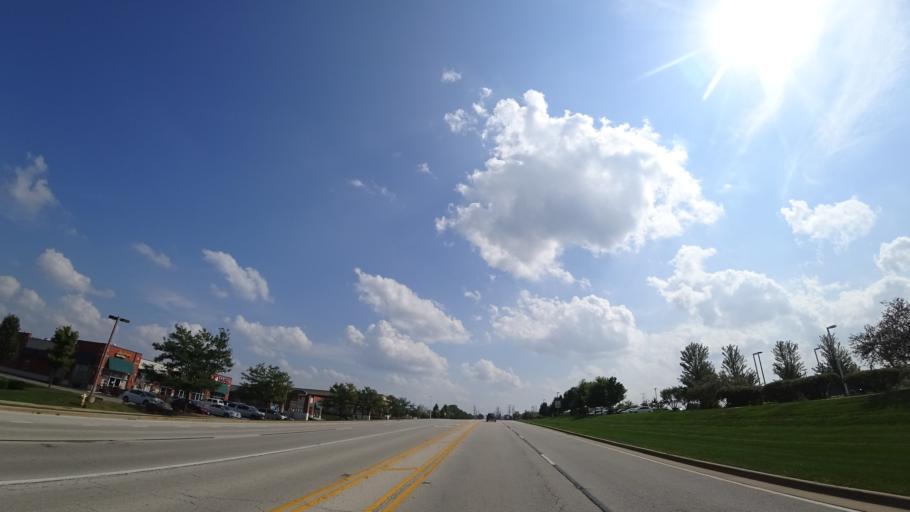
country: US
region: Illinois
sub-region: Will County
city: Goodings Grove
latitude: 41.6360
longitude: -87.9313
